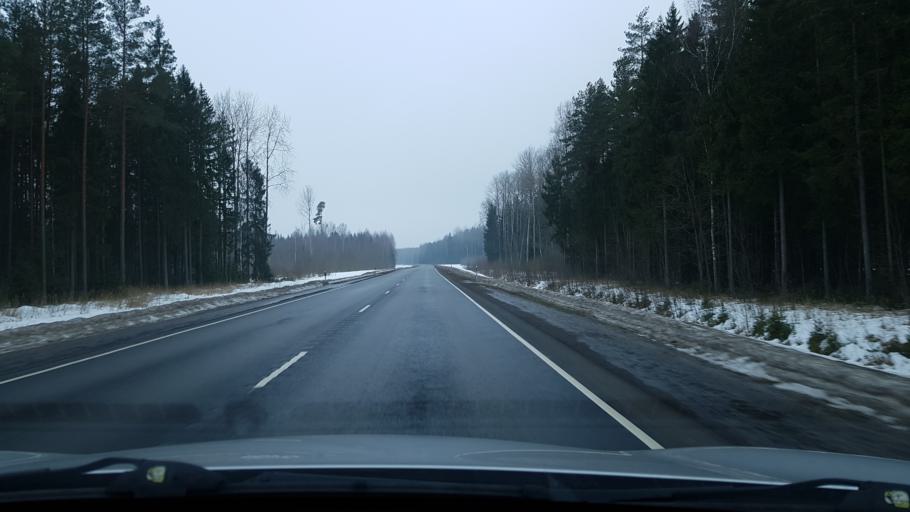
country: EE
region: Valgamaa
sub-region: Valga linn
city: Valga
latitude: 57.8745
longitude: 26.1556
